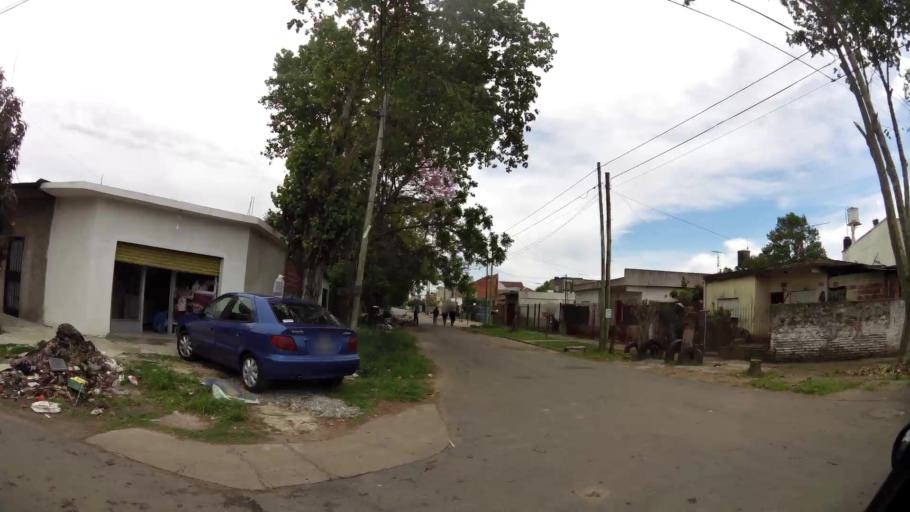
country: AR
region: Buenos Aires
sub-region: Partido de Quilmes
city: Quilmes
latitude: -34.7599
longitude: -58.2314
